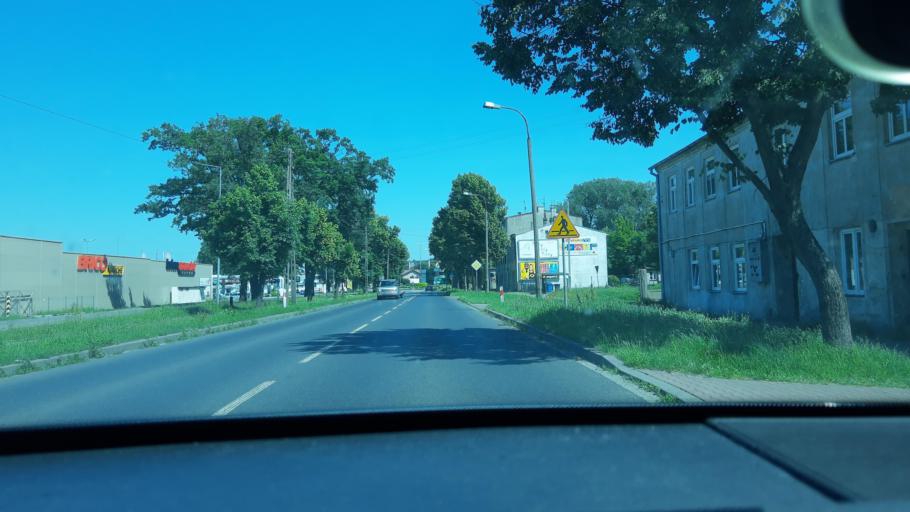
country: PL
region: Lodz Voivodeship
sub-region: Powiat zdunskowolski
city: Zdunska Wola
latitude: 51.6072
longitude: 18.9172
